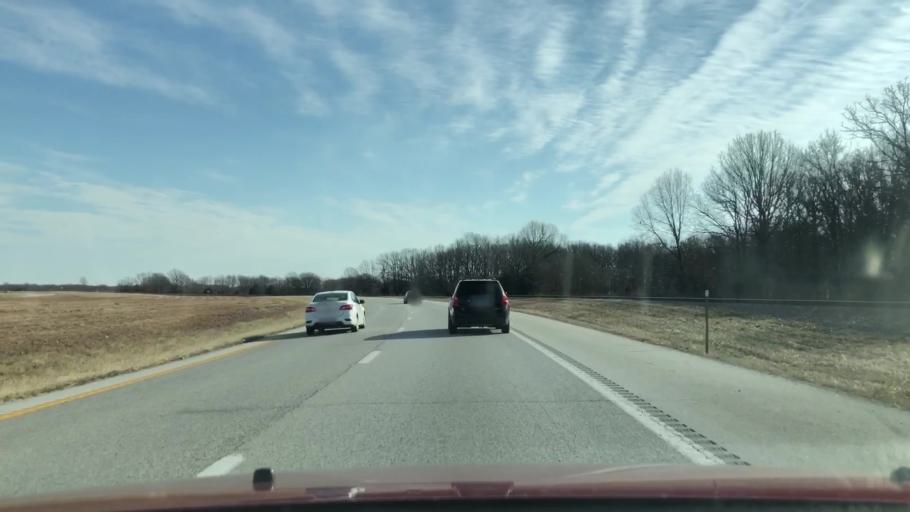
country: US
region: Missouri
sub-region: Webster County
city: Seymour
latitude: 37.1297
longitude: -92.7370
